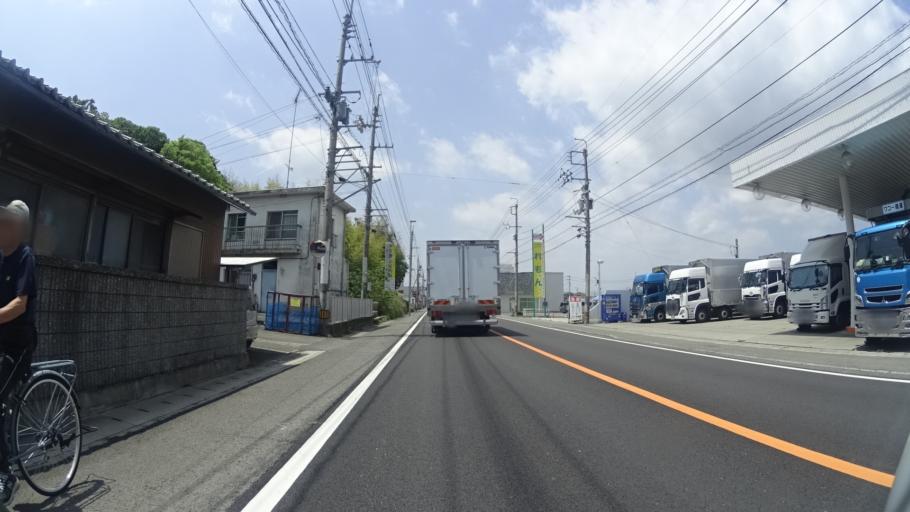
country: JP
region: Tokushima
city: Ishii
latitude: 34.0704
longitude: 134.4641
